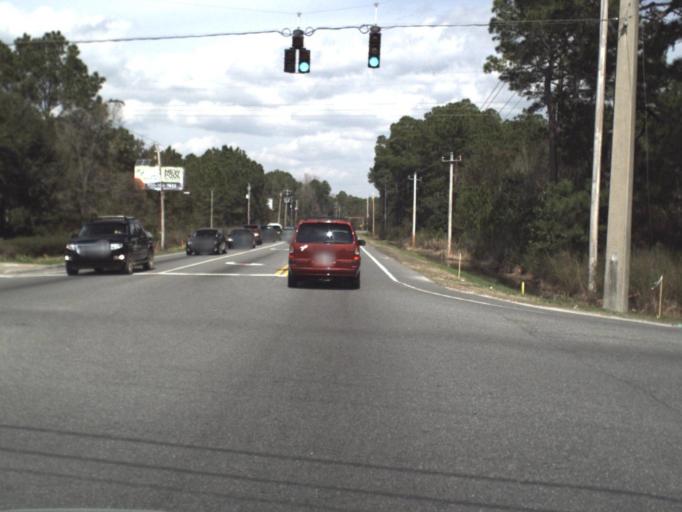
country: US
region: Florida
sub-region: Bay County
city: Lynn Haven
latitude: 30.2230
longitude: -85.6628
